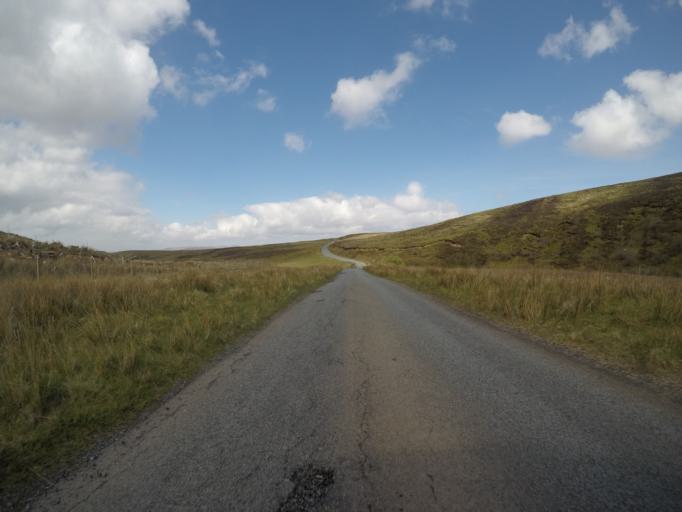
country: GB
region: Scotland
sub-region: Highland
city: Isle of Skye
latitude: 57.4146
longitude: -6.2970
